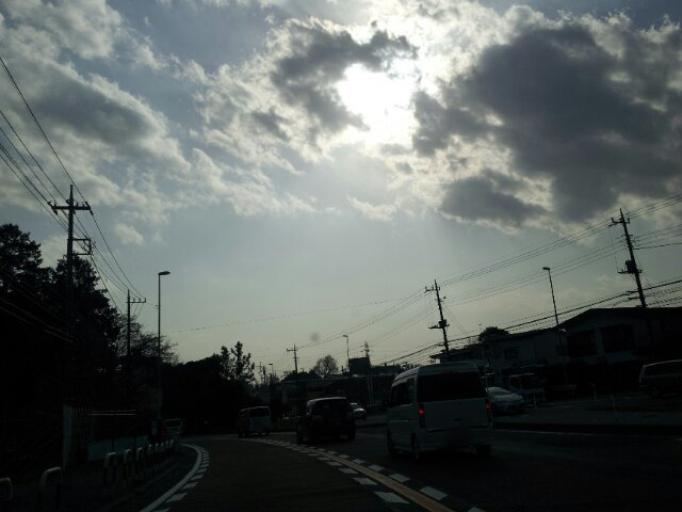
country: JP
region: Kanagawa
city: Fujisawa
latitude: 35.3877
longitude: 139.5190
